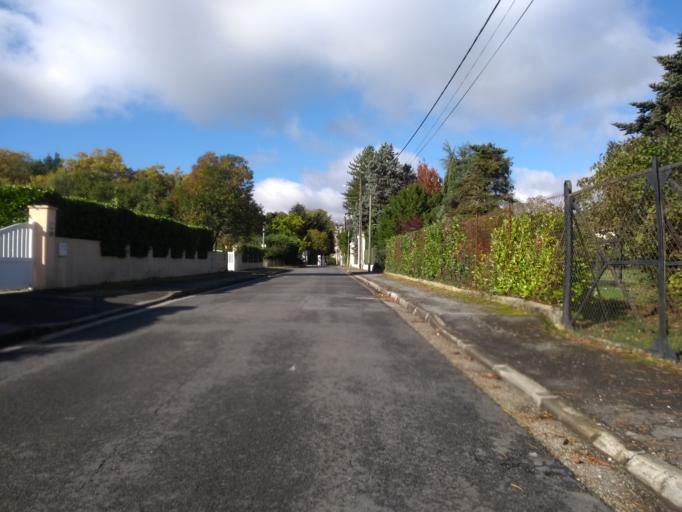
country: FR
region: Aquitaine
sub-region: Departement de la Gironde
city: Canejan
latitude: 44.7742
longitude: -0.6280
